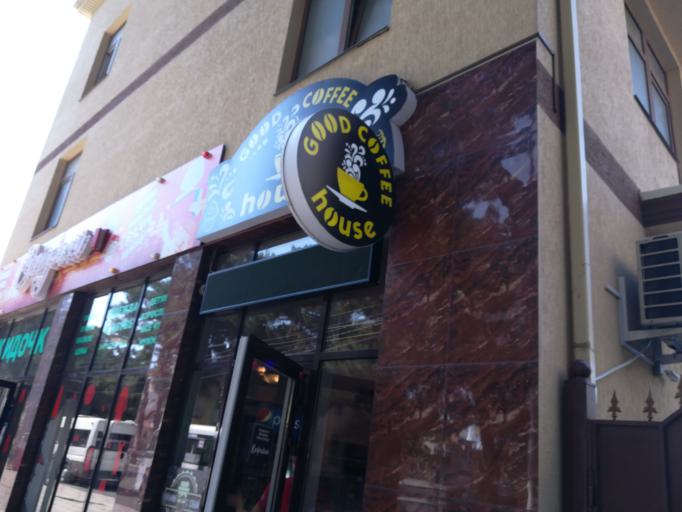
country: RU
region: Krasnodarskiy
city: Anapa
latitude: 44.8953
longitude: 37.3193
